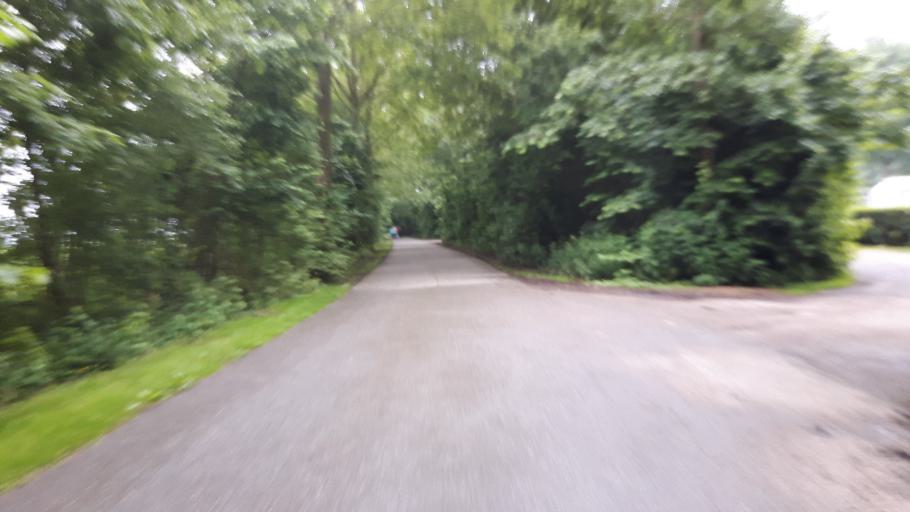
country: NL
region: Utrecht
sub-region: Gemeente Lopik
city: Lopik
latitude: 51.9711
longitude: 4.9590
